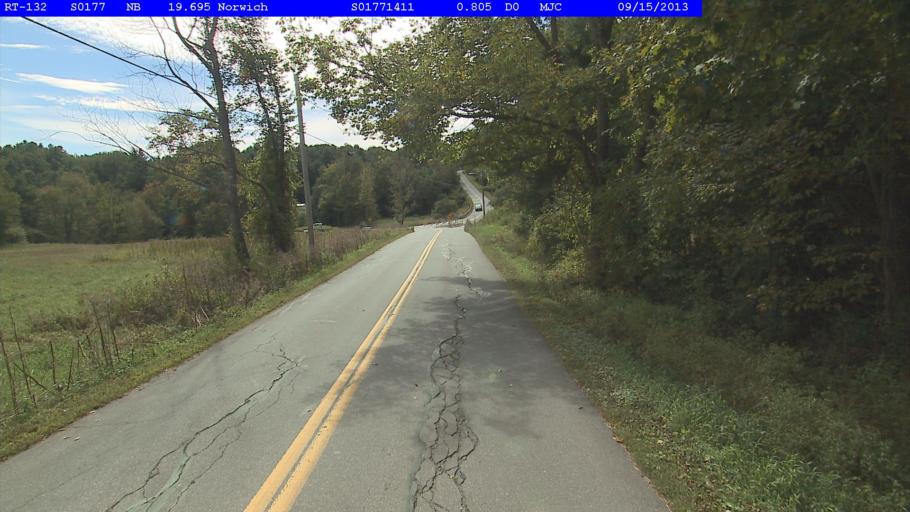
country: US
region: New Hampshire
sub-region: Grafton County
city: Hanover
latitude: 43.7752
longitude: -72.2582
